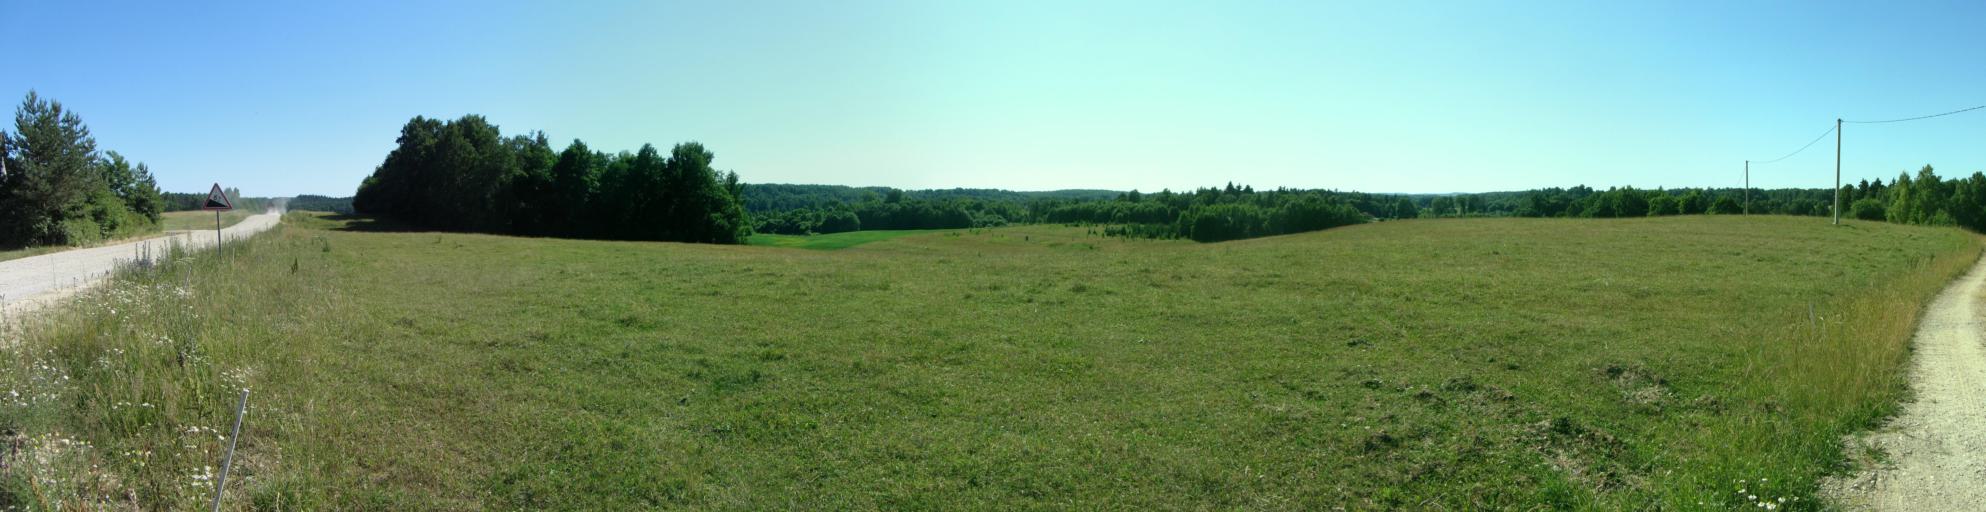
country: LT
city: Aukstadvaris
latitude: 54.5873
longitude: 24.6461
